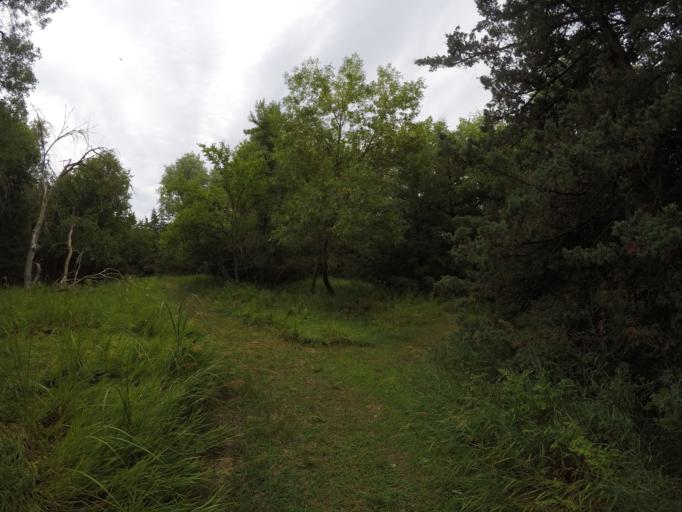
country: US
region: Nebraska
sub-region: Buffalo County
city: Kearney
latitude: 40.6582
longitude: -99.0109
